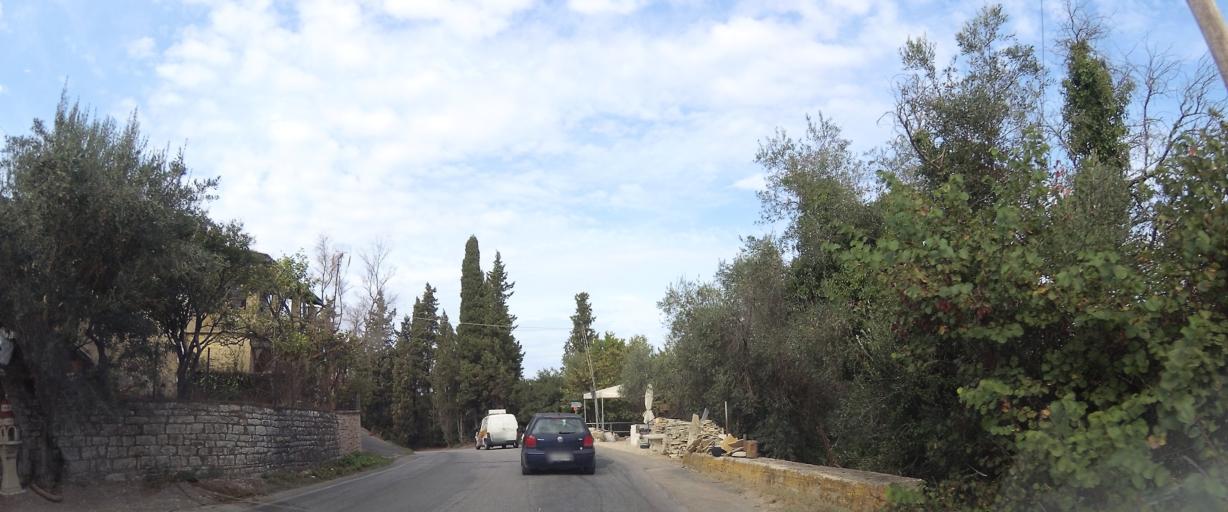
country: GR
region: Ionian Islands
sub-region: Nomos Kerkyras
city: Acharavi
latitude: 39.7673
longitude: 19.9333
